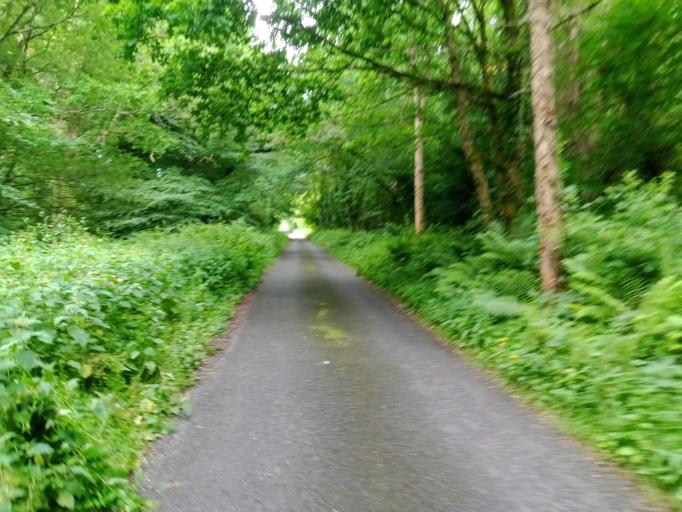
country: IE
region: Leinster
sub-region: Kilkenny
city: Piltown
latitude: 52.4554
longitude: -7.2766
